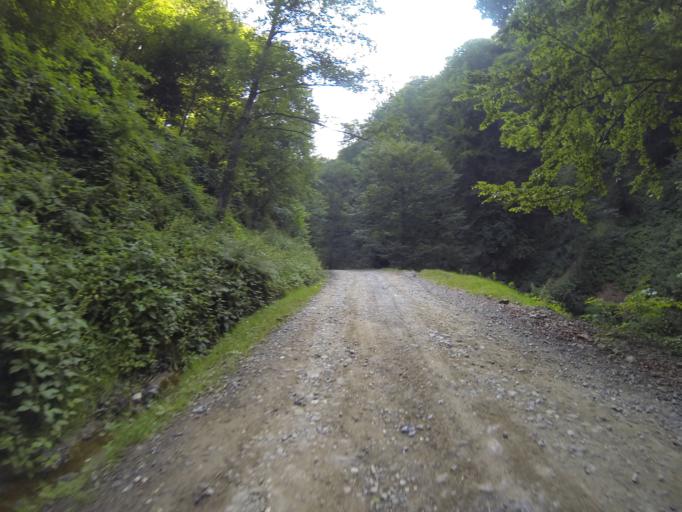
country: RO
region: Valcea
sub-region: Comuna Costesti
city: Bistrita
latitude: 45.2126
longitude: 24.0055
